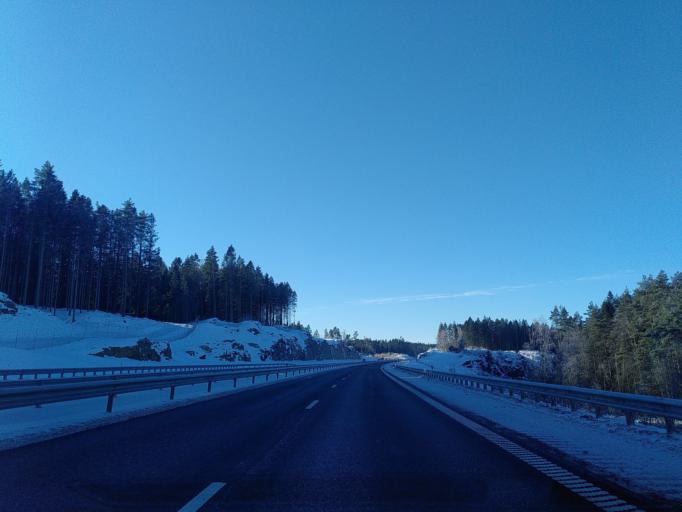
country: SE
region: Vaestra Goetaland
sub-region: Vargarda Kommun
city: Jonstorp
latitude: 57.9783
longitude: 12.7109
